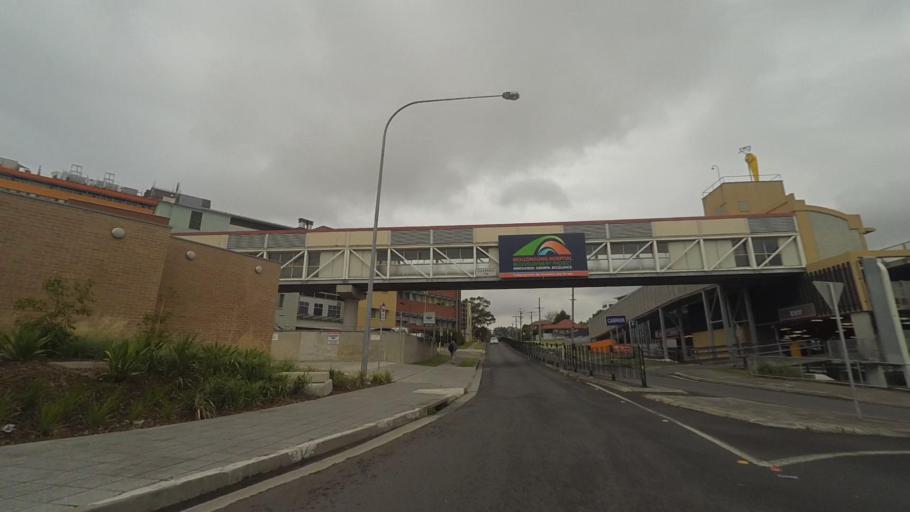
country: AU
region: New South Wales
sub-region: Wollongong
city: Gwynneville
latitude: -34.4240
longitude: 150.8828
